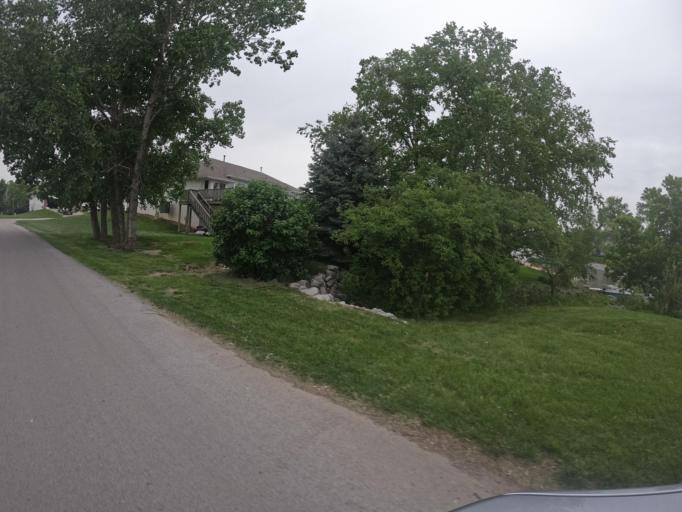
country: US
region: Nebraska
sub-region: Sarpy County
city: Offutt Air Force Base
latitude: 41.0498
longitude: -95.9525
